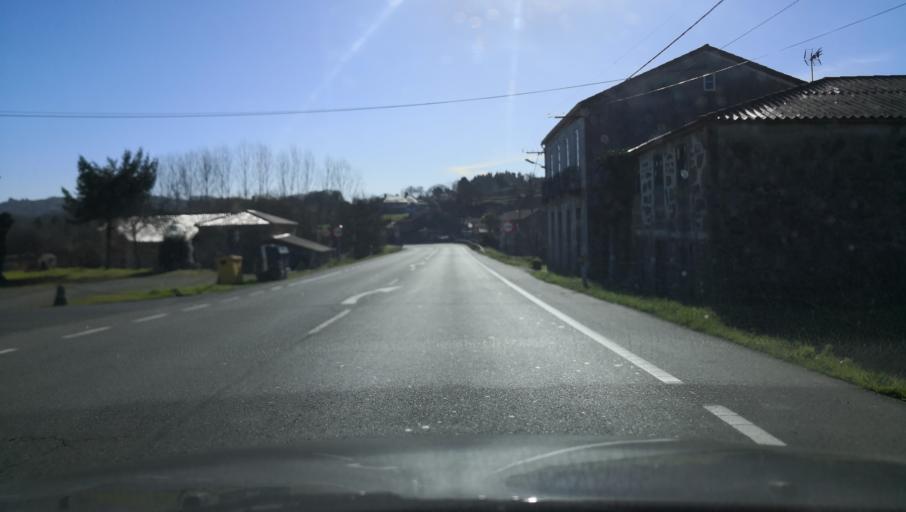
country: ES
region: Galicia
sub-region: Provincia de Pontevedra
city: Silleda
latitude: 42.7247
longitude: -8.2972
